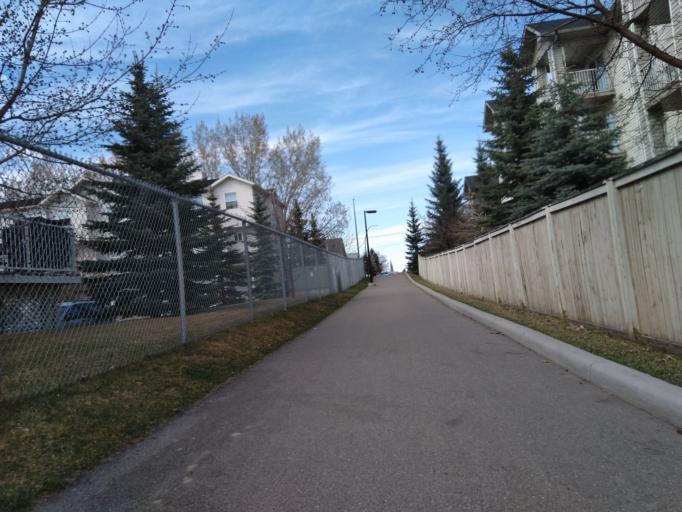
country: CA
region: Alberta
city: Chestermere
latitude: 51.0391
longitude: -113.9303
